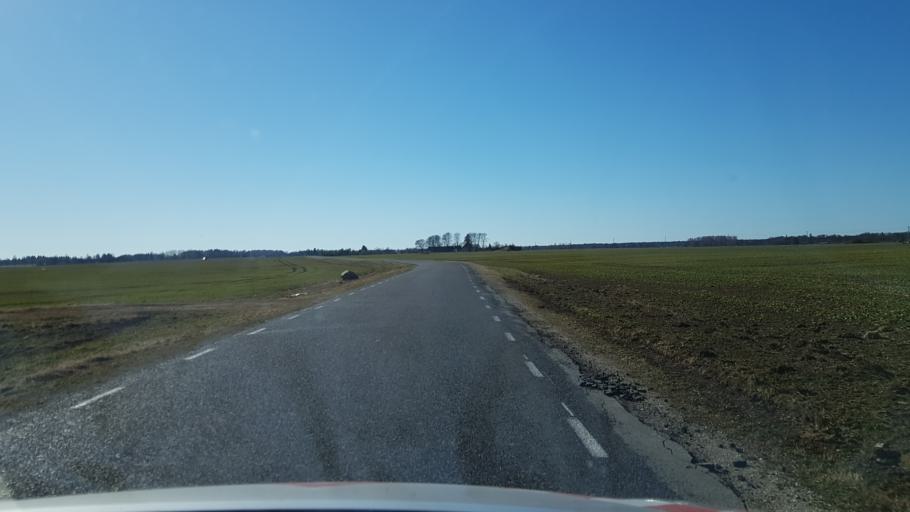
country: EE
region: Laeaene-Virumaa
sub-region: Haljala vald
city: Haljala
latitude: 59.4348
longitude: 26.2216
